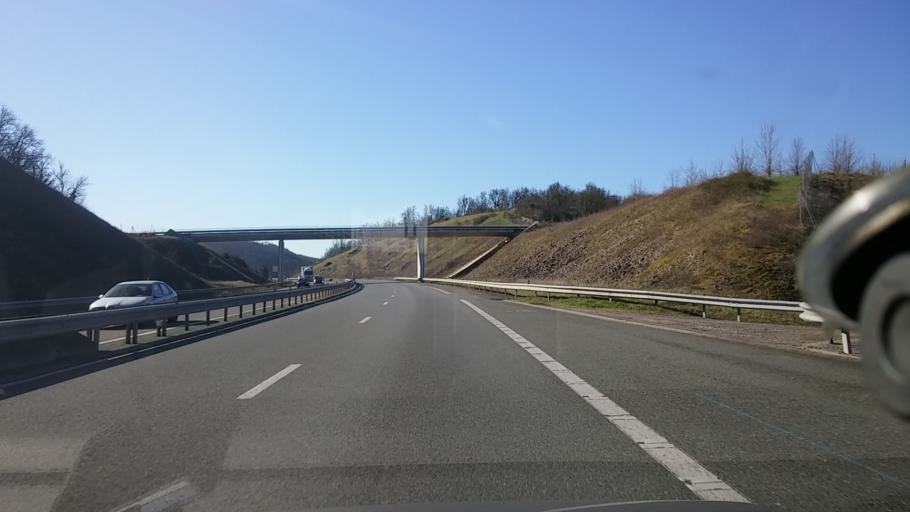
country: FR
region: Midi-Pyrenees
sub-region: Departement du Lot
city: Souillac
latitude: 44.8438
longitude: 1.4911
